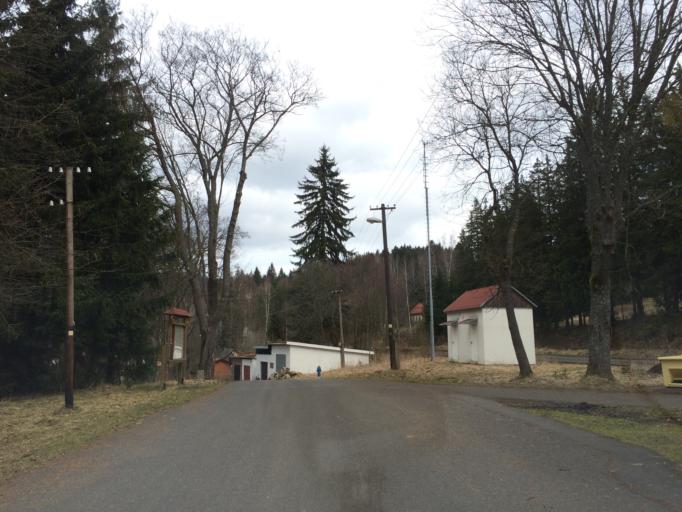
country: CZ
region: Karlovarsky
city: Nejdek
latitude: 50.3572
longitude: 12.7191
